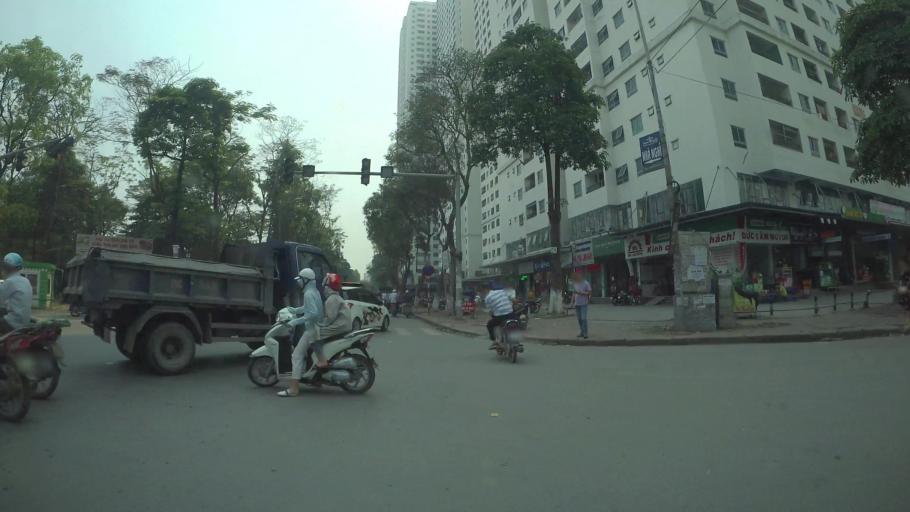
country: VN
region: Ha Noi
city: Van Dien
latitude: 20.9649
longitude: 105.8257
